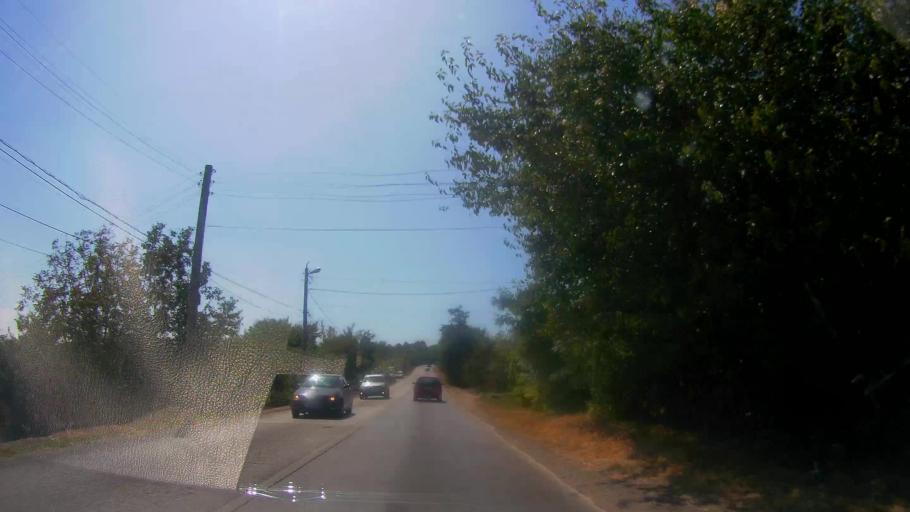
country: BG
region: Veliko Turnovo
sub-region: Obshtina Gorna Oryakhovitsa
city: Purvomaytsi
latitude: 43.1724
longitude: 25.6205
